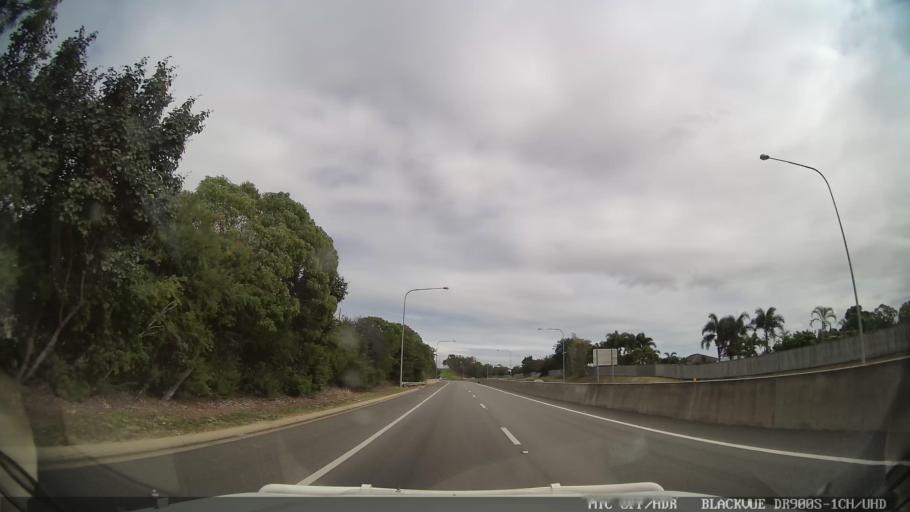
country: AU
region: Queensland
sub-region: Townsville
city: Bohle Plains
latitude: -19.3211
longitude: 146.7462
